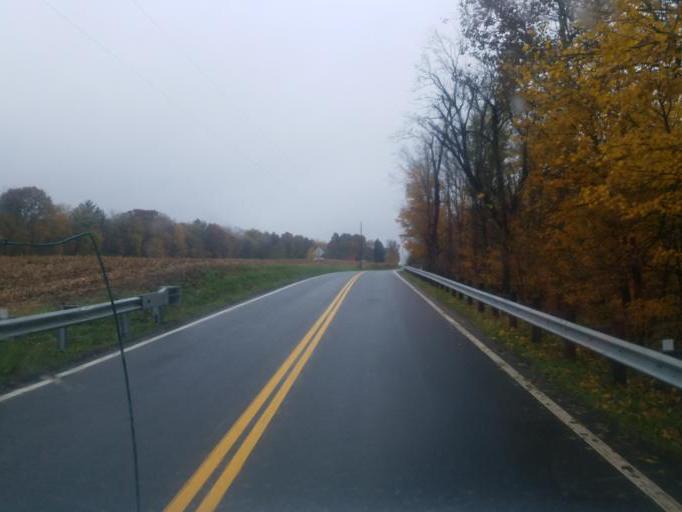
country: US
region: Ohio
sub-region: Richland County
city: Lexington
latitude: 40.6395
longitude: -82.6633
